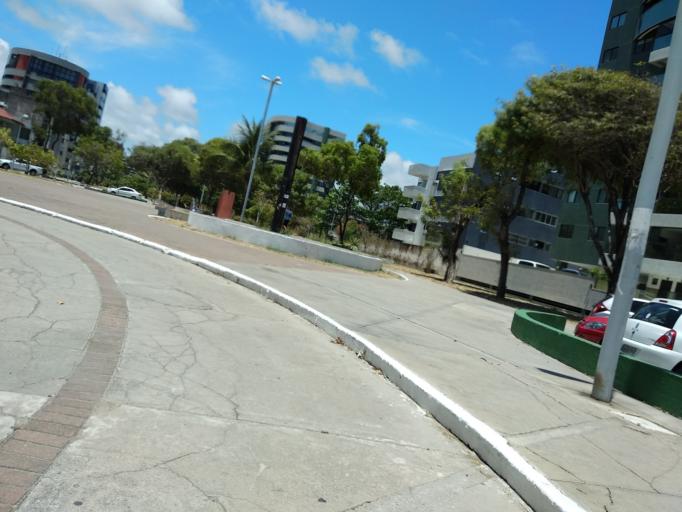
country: BR
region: Alagoas
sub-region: Maceio
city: Maceio
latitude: -9.6473
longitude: -35.7023
